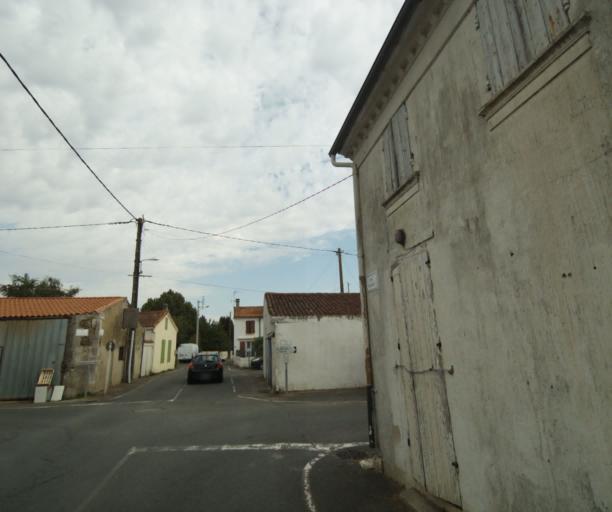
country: FR
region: Poitou-Charentes
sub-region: Departement de la Charente-Maritime
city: Tonnay-Charente
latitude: 45.9658
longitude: -0.8720
